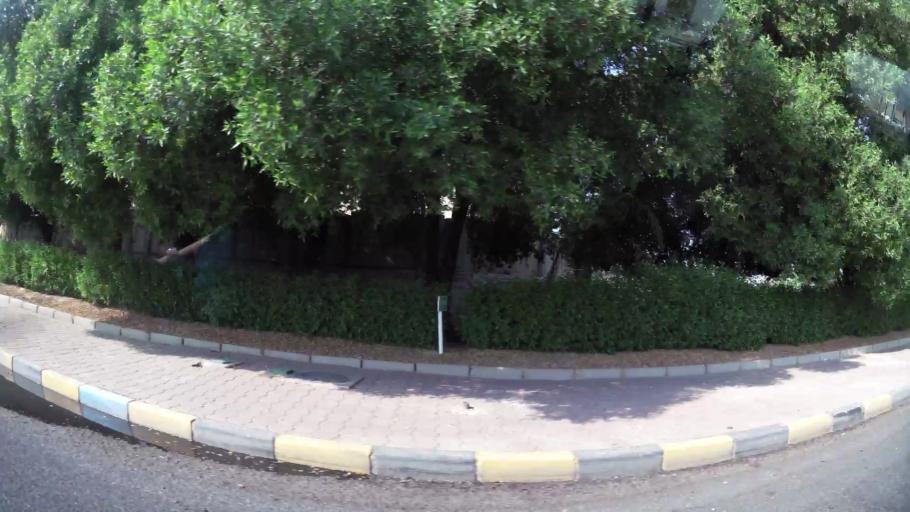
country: KW
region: Al Asimah
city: Ar Rabiyah
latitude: 29.2778
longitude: 47.9069
